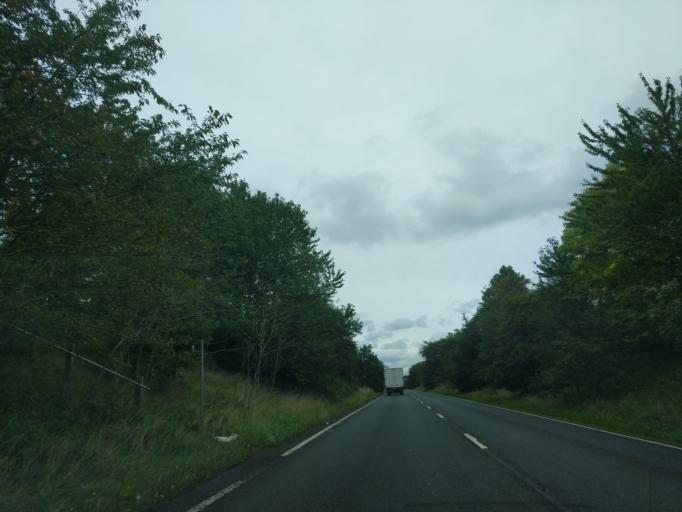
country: GB
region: England
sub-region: Cheshire East
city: Weston
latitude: 53.0619
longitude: -2.3935
